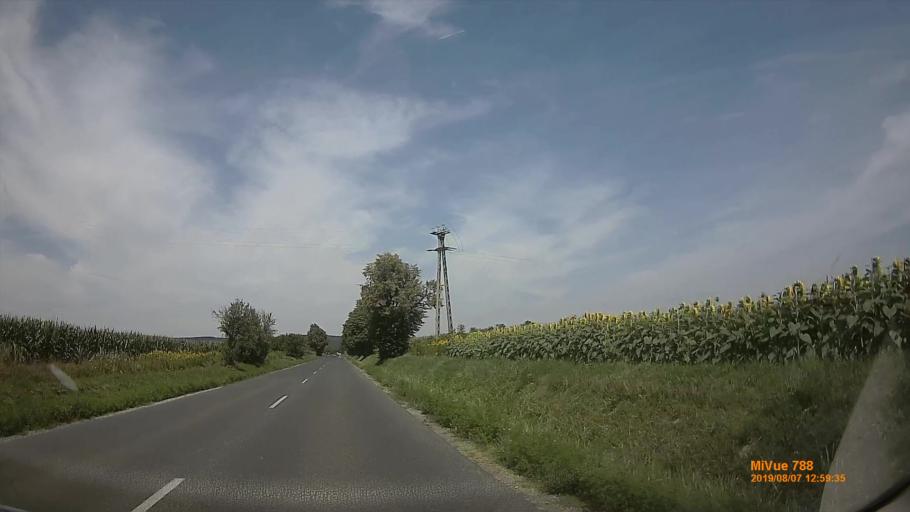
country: HU
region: Zala
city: Keszthely
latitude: 46.7867
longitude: 17.2398
